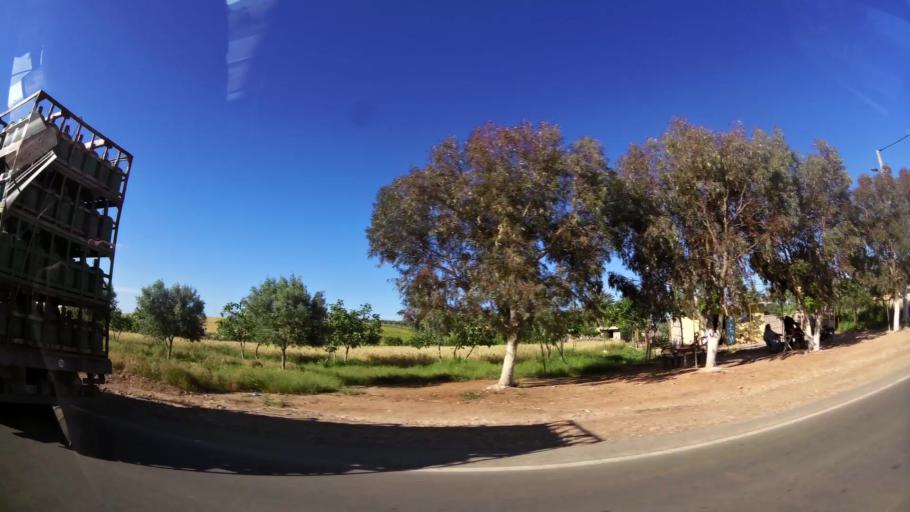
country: MA
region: Oriental
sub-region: Berkane-Taourirt
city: Ahfir
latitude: 34.9756
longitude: -2.1297
